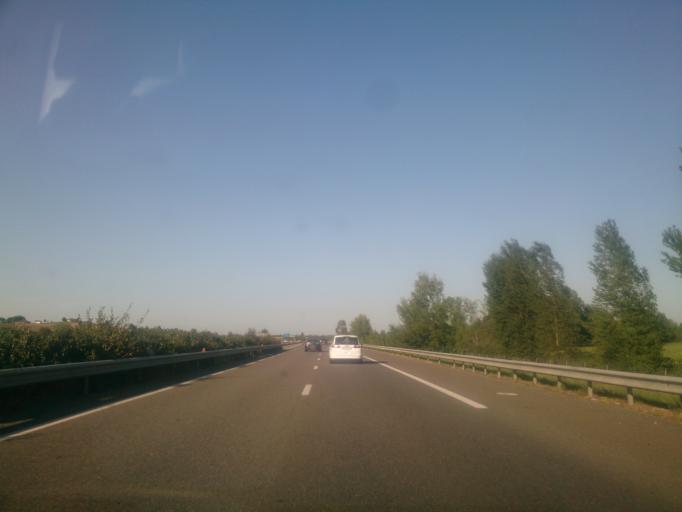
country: FR
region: Midi-Pyrenees
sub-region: Departement du Tarn-et-Garonne
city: Caussade
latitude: 44.1462
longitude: 1.5063
